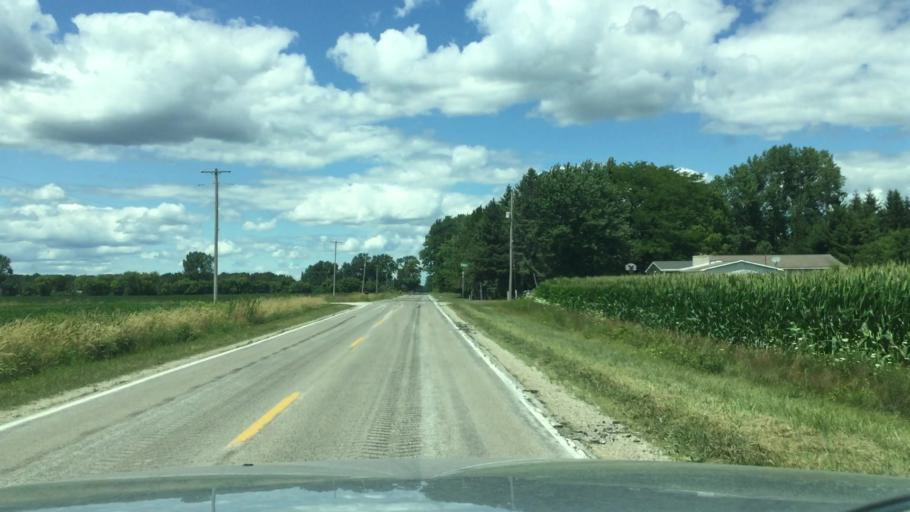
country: US
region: Michigan
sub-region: Saginaw County
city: Saint Charles
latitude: 43.3411
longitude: -84.1898
